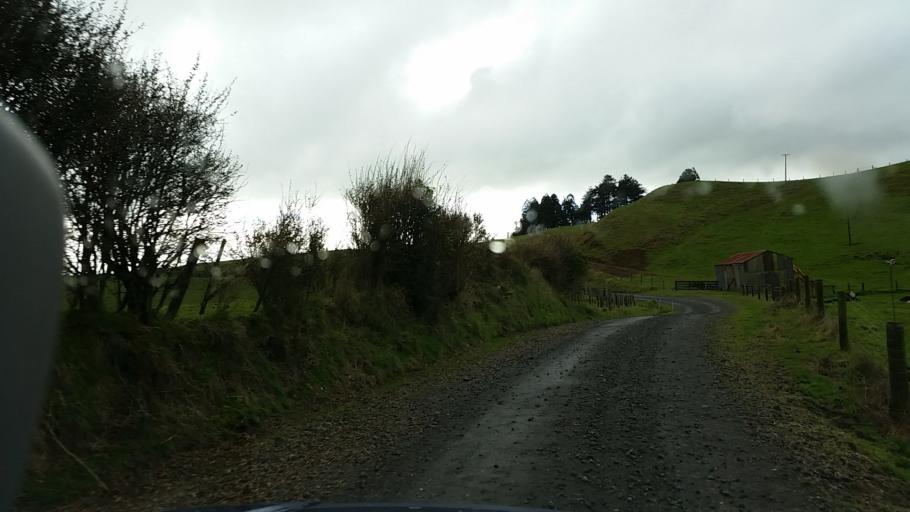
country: NZ
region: Taranaki
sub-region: South Taranaki District
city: Eltham
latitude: -39.2797
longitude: 174.3382
